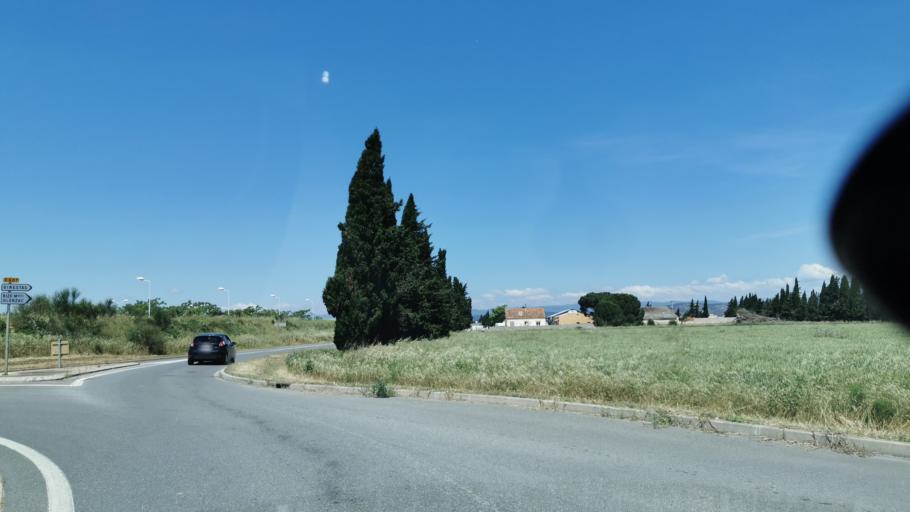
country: FR
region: Languedoc-Roussillon
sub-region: Departement de l'Aude
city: Saint-Marcel-sur-Aude
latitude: 43.2562
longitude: 2.9106
